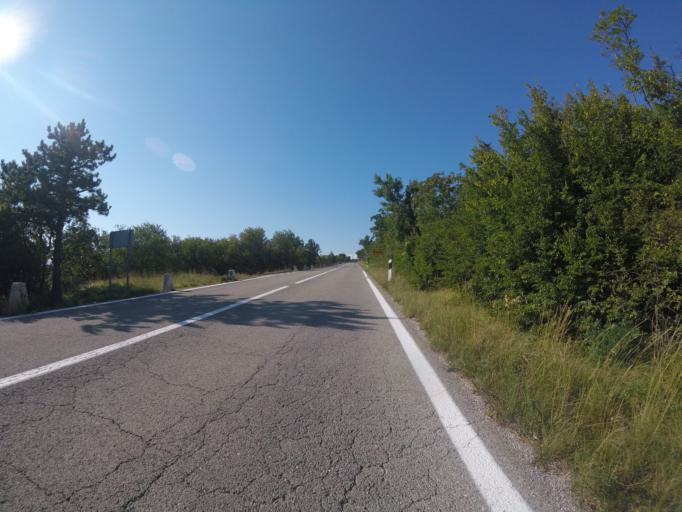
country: HR
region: Primorsko-Goranska
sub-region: Grad Crikvenica
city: Jadranovo
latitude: 45.2510
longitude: 14.6071
